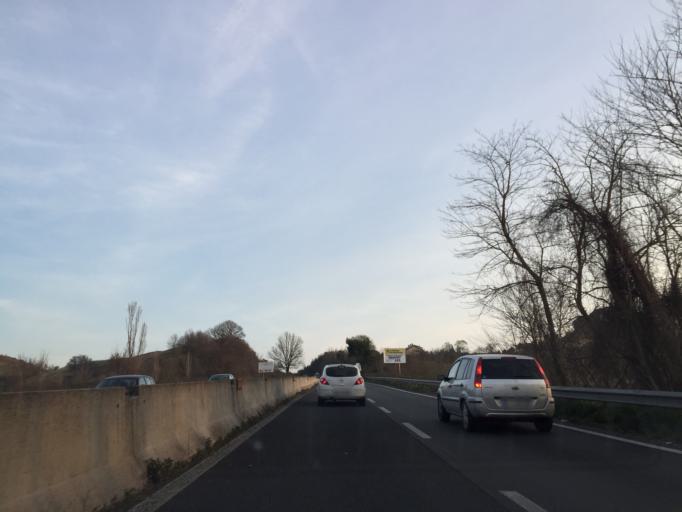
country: IT
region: Latium
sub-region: Citta metropolitana di Roma Capitale
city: Campagnano di Roma
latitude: 42.1394
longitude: 12.3518
